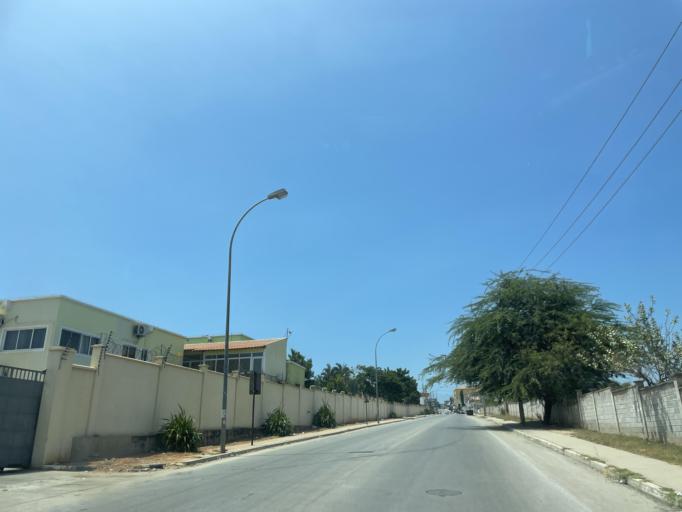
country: AO
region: Luanda
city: Luanda
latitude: -8.9174
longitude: 13.2041
